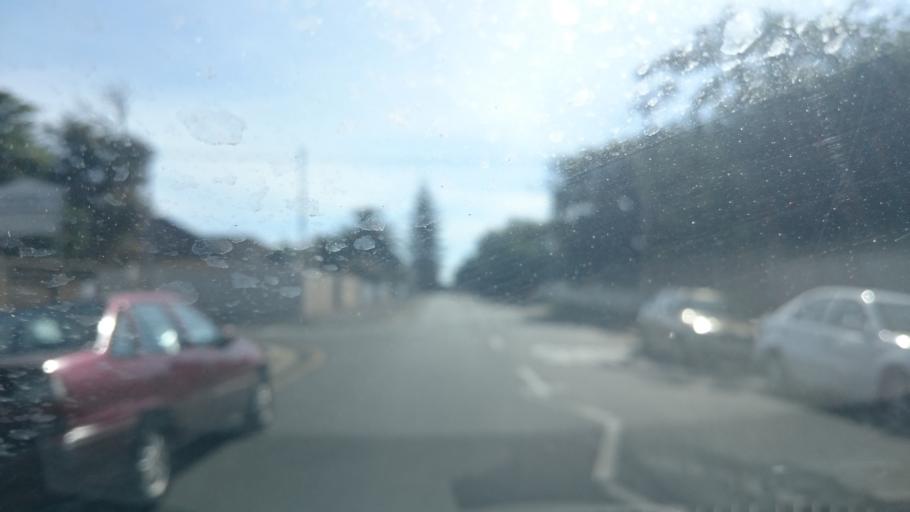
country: ZA
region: Western Cape
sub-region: City of Cape Town
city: Bergvliet
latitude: -34.0198
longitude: 18.4739
